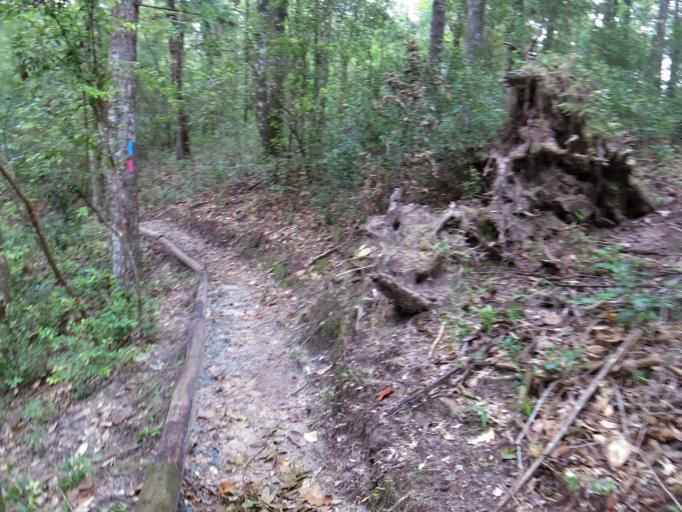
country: US
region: Florida
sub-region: Clay County
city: Middleburg
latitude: 30.1417
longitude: -81.9527
